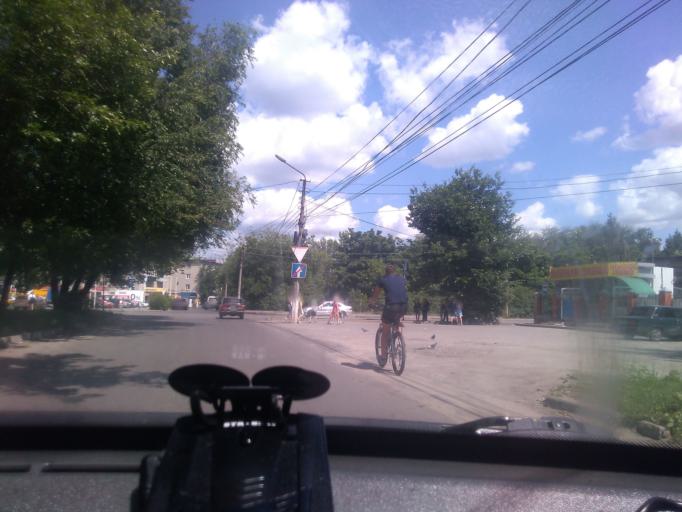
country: RU
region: Kursk
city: Voroshnevo
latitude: 51.6689
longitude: 36.0733
